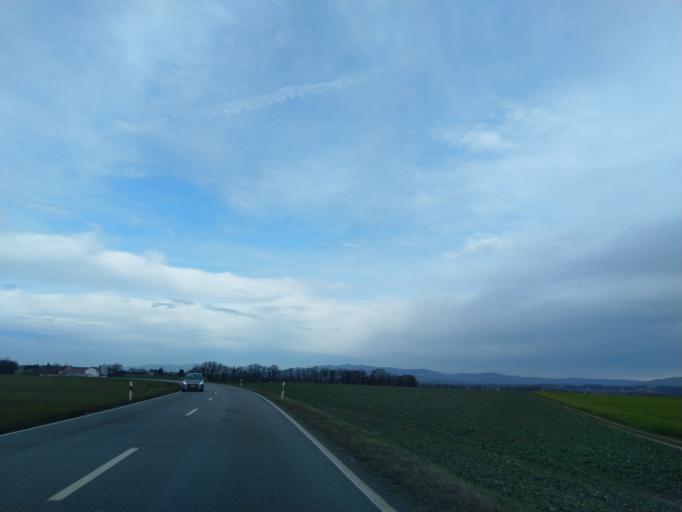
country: DE
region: Bavaria
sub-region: Lower Bavaria
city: Kunzing
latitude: 48.6586
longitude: 13.0453
